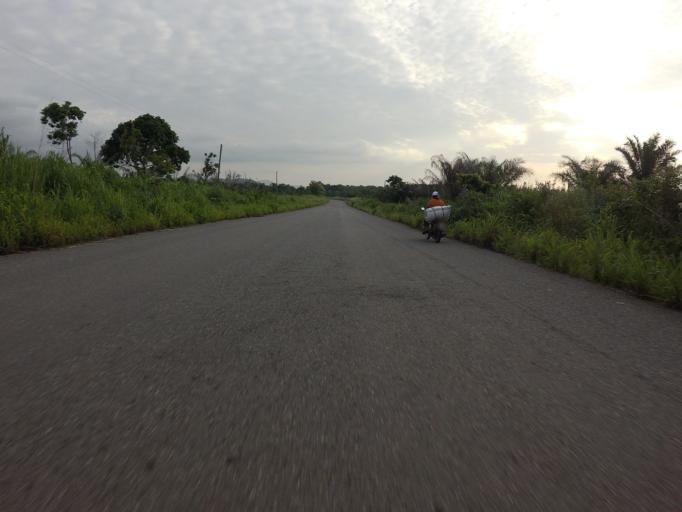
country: GH
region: Volta
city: Kpandu
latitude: 6.8674
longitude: 0.4062
